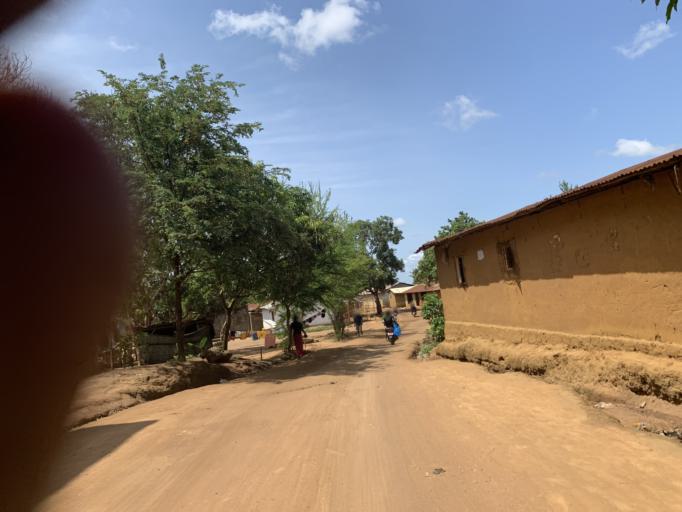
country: SL
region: Western Area
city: Waterloo
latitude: 8.3398
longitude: -13.0489
